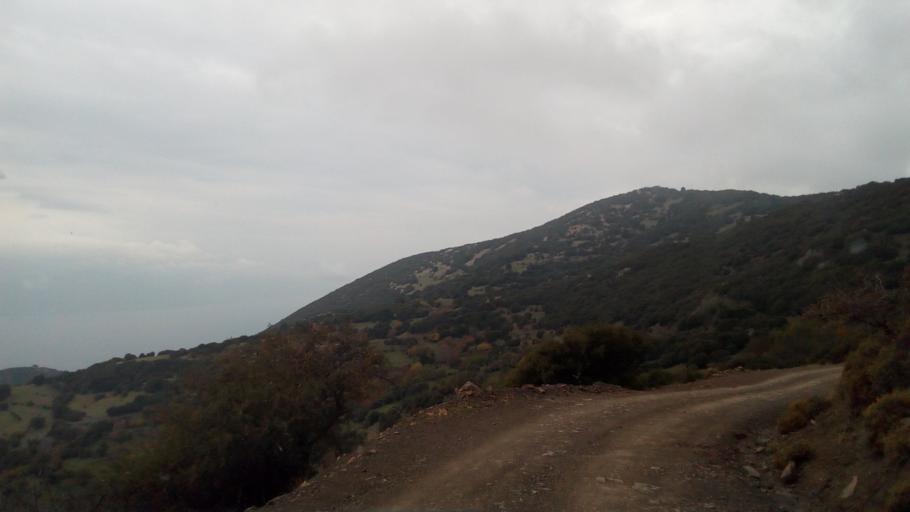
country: GR
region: West Greece
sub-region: Nomos Achaias
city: Selianitika
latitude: 38.4158
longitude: 22.0957
